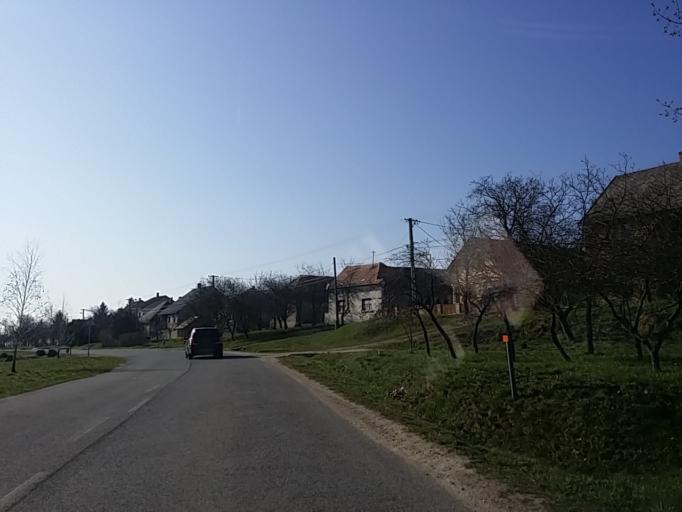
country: HU
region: Fejer
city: Szarliget
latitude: 47.4815
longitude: 18.5135
